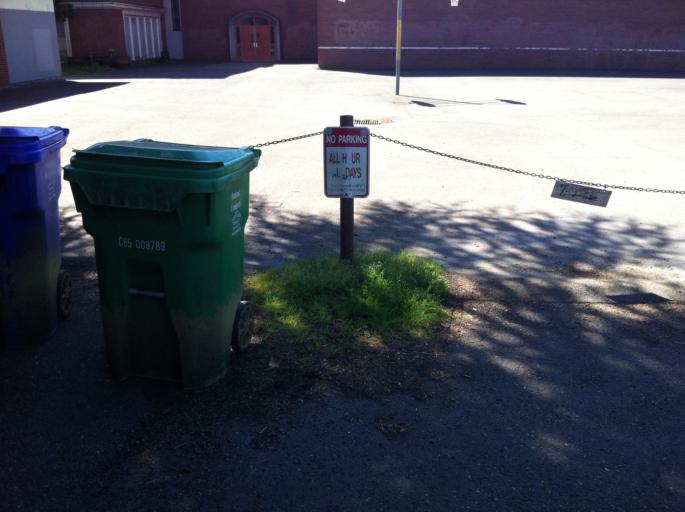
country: US
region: Oregon
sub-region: Multnomah County
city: Lents
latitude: 45.4989
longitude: -122.5909
